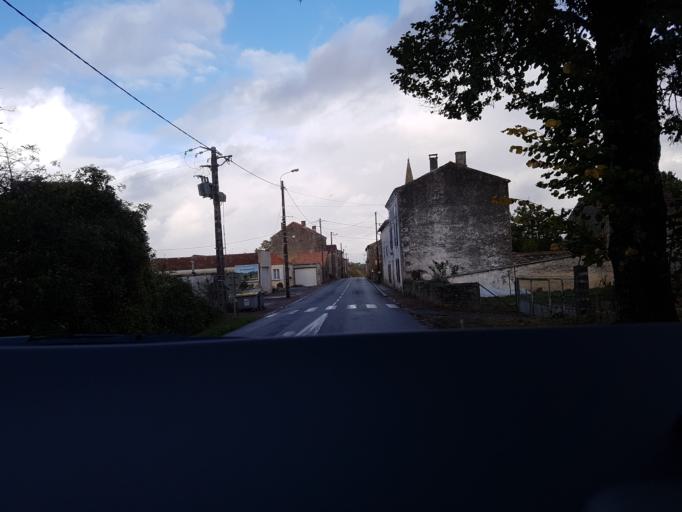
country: FR
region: Poitou-Charentes
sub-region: Departement de la Charente-Maritime
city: Aulnay
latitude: 46.0601
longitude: -0.3234
